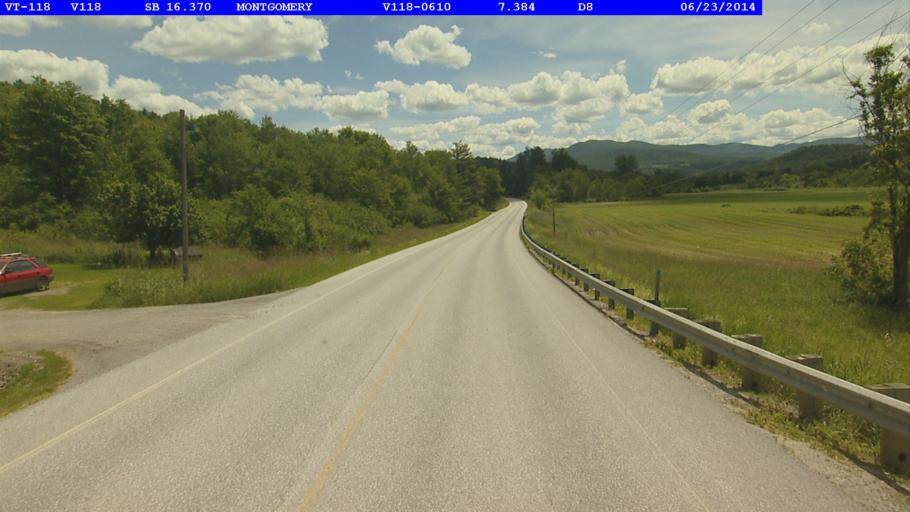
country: US
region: Vermont
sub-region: Franklin County
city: Richford
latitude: 44.8971
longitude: -72.6291
